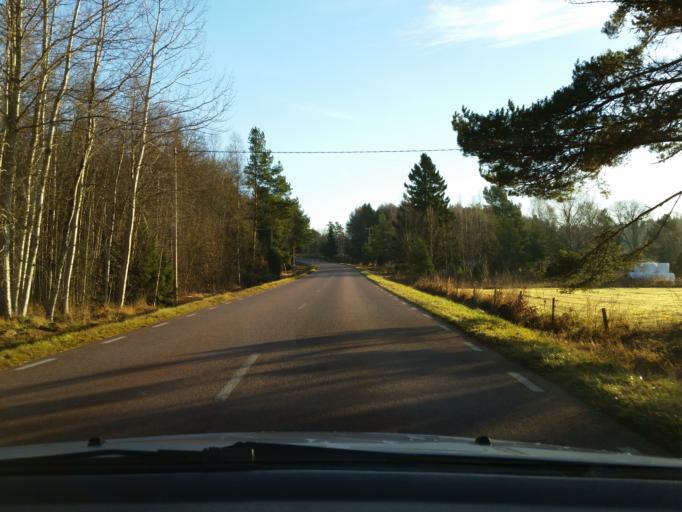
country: AX
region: Alands landsbygd
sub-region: Sund
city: Sund
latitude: 60.2800
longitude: 20.1011
